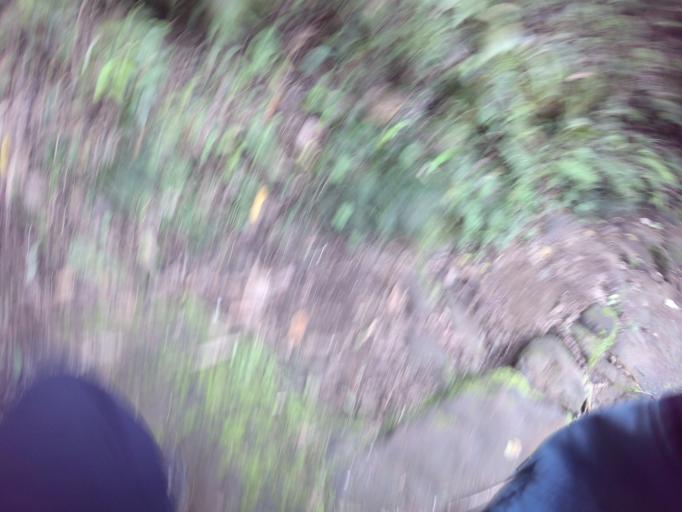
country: CO
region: Cundinamarca
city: San Antonio del Tequendama
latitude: 4.6097
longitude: -74.3097
